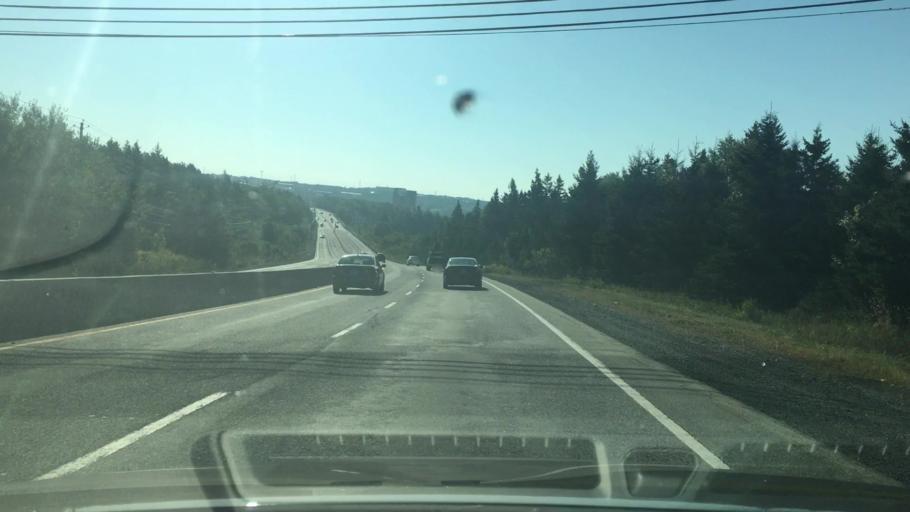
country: CA
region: Nova Scotia
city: Dartmouth
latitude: 44.7091
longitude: -63.6249
